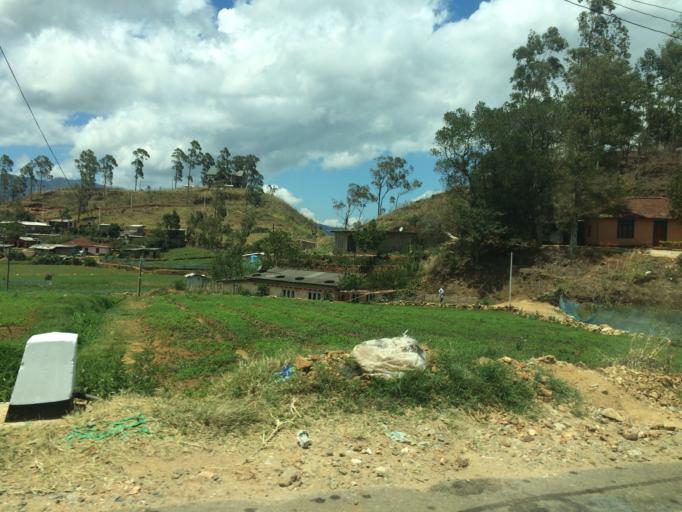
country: LK
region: Central
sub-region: Nuwara Eliya District
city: Nuwara Eliya
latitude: 6.9051
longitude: 80.8466
